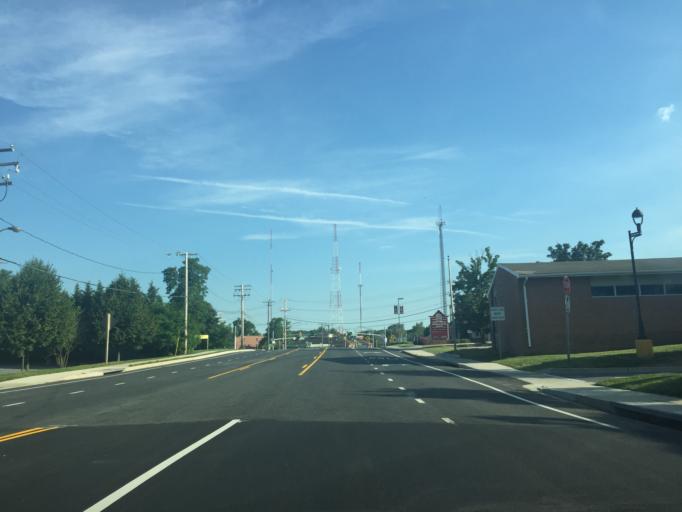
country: US
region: Maryland
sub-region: Baltimore County
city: Hunt Valley
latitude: 39.5200
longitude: -76.5593
